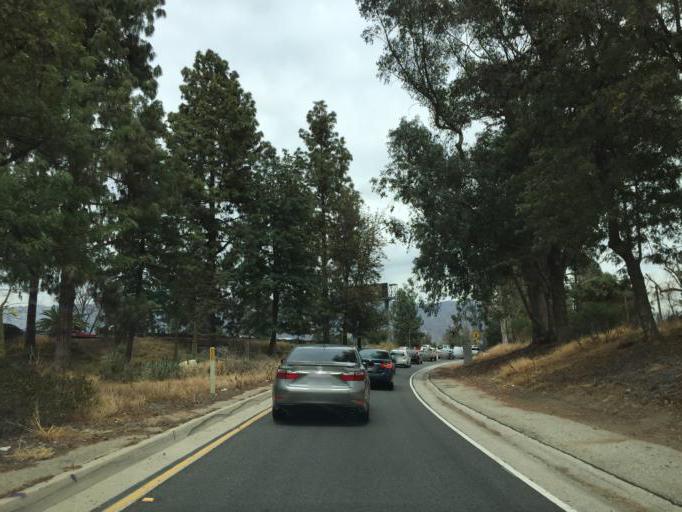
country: US
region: California
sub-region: Los Angeles County
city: Burbank
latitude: 34.1544
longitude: -118.3108
